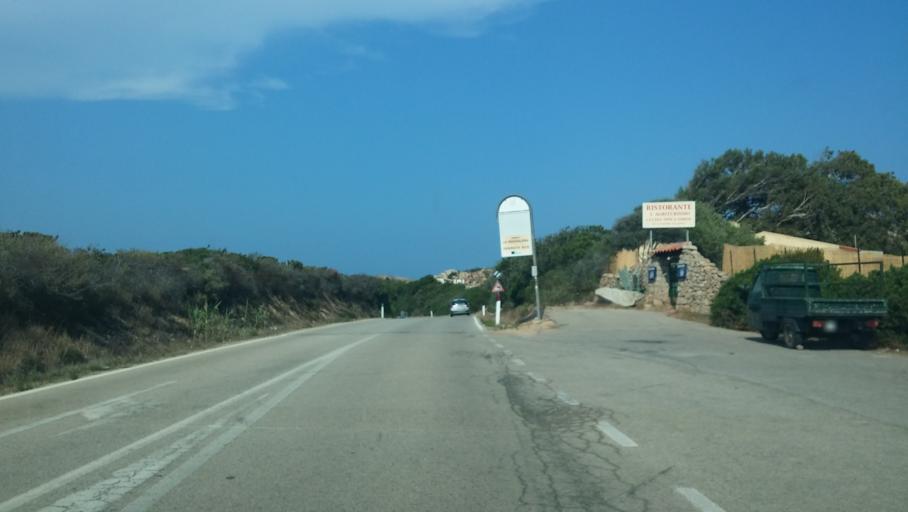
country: IT
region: Sardinia
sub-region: Provincia di Olbia-Tempio
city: La Maddalena
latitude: 41.2405
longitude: 9.4275
